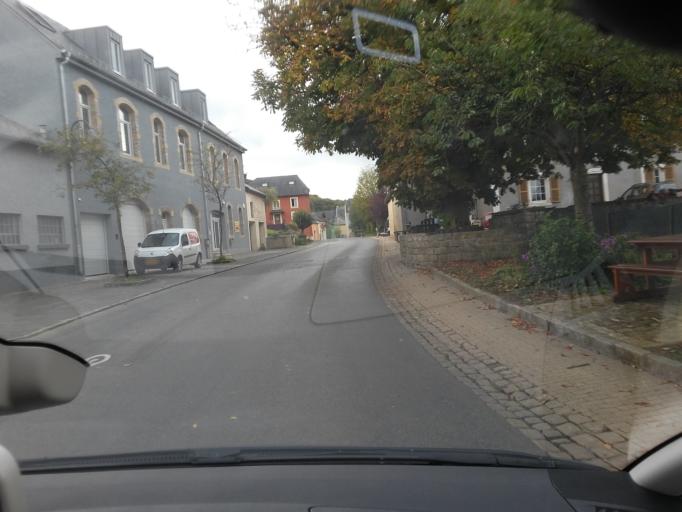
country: LU
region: Diekirch
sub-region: Canton de Redange
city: Beckerich
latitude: 49.7308
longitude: 5.8814
